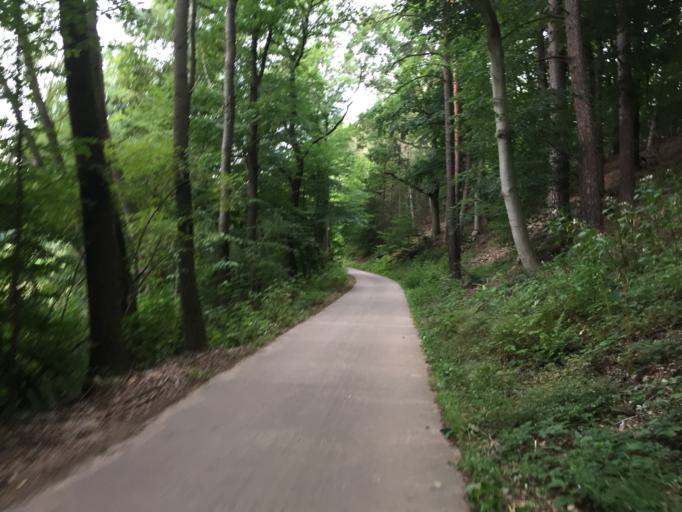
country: DE
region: Hesse
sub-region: Regierungsbezirk Kassel
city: Bad Hersfeld
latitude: 50.8865
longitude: 9.7417
